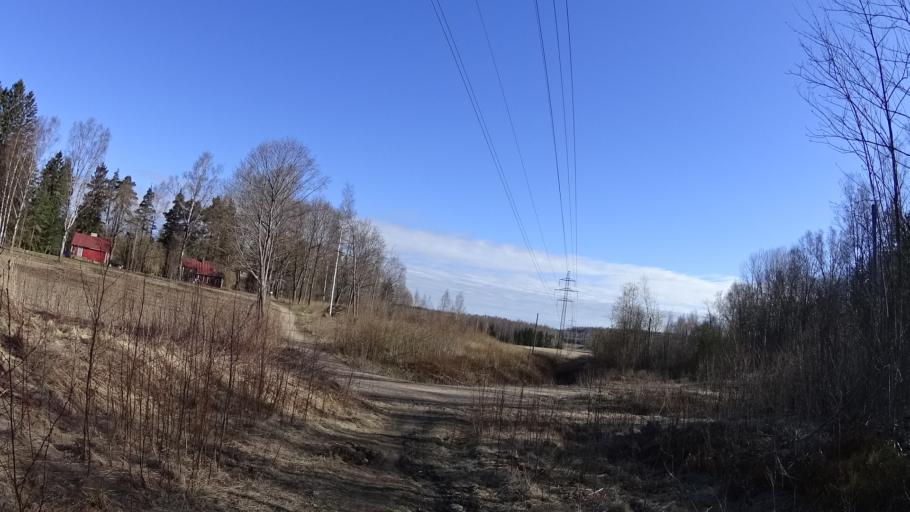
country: FI
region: Uusimaa
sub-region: Helsinki
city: Kilo
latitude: 60.2343
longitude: 24.7882
